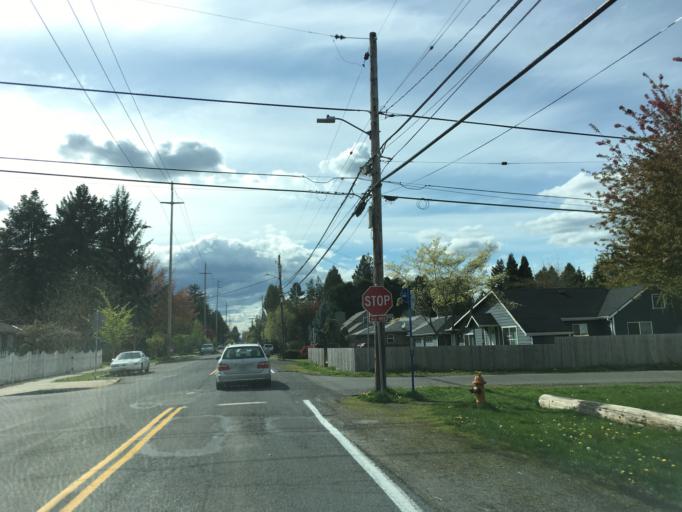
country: US
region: Oregon
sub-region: Multnomah County
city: Lents
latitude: 45.5555
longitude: -122.5440
